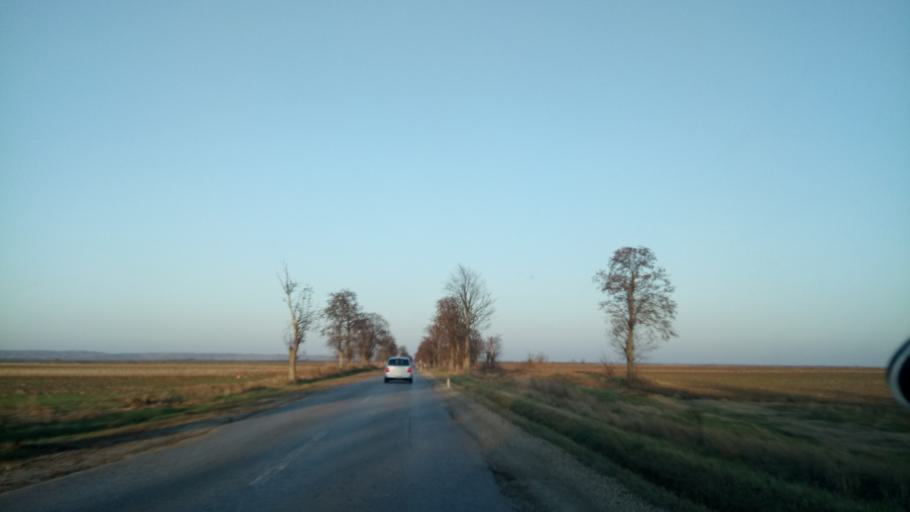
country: RS
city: Novi Karlovci
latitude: 45.0927
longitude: 20.1957
